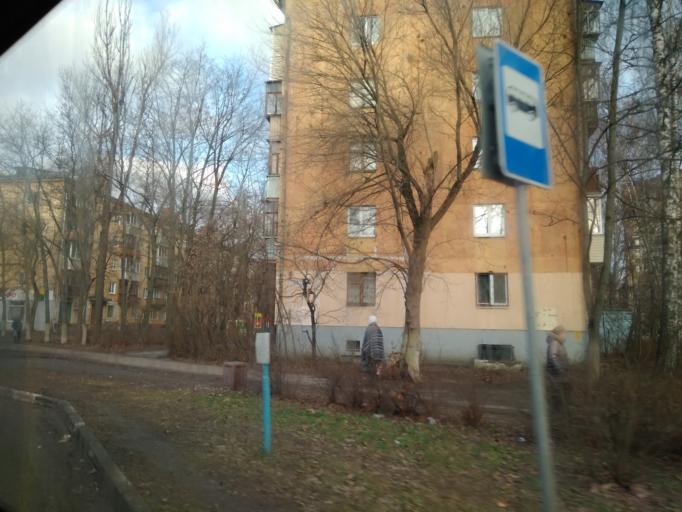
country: RU
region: Moskovskaya
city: Zhukovskiy
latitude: 55.5921
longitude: 38.1295
